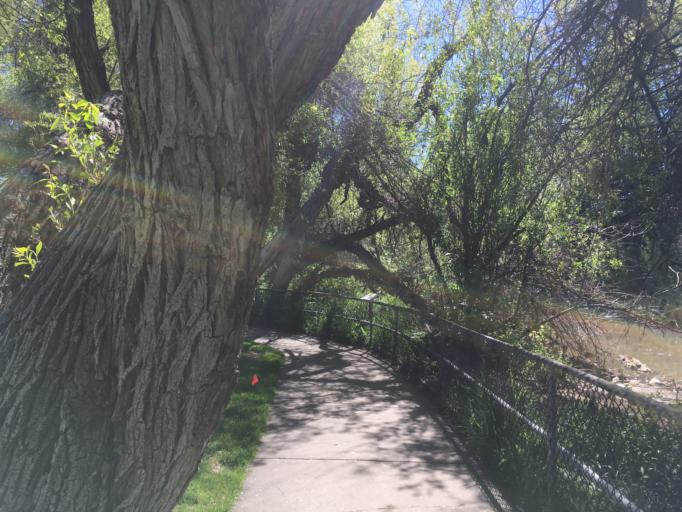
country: US
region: Utah
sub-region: Davis County
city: Layton
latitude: 41.0657
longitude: -111.9637
